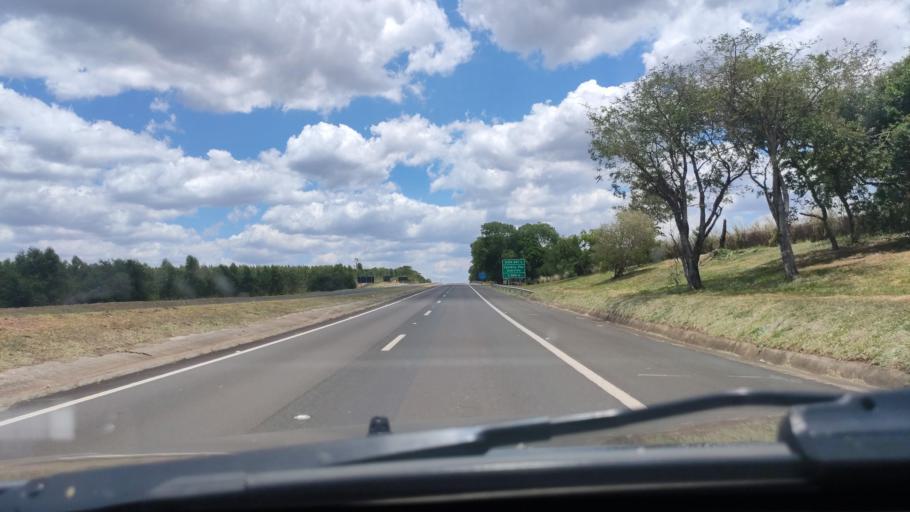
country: BR
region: Sao Paulo
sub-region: Duartina
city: Duartina
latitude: -22.5064
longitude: -49.2901
